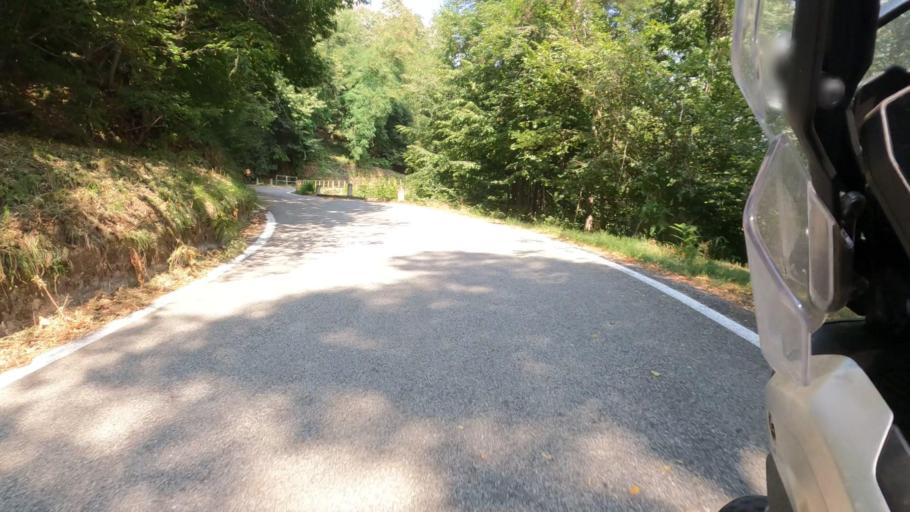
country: IT
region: Lombardy
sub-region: Provincia di Varese
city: Veddasca
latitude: 46.0593
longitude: 8.7808
